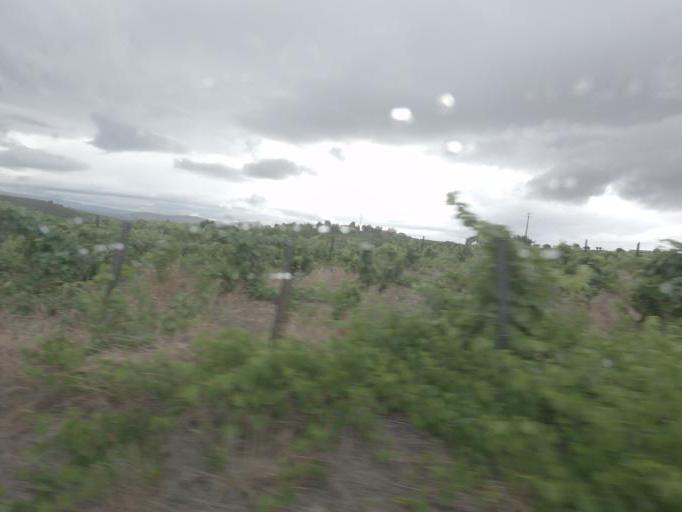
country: PT
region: Vila Real
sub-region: Sabrosa
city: Sabrosa
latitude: 41.2456
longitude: -7.4984
